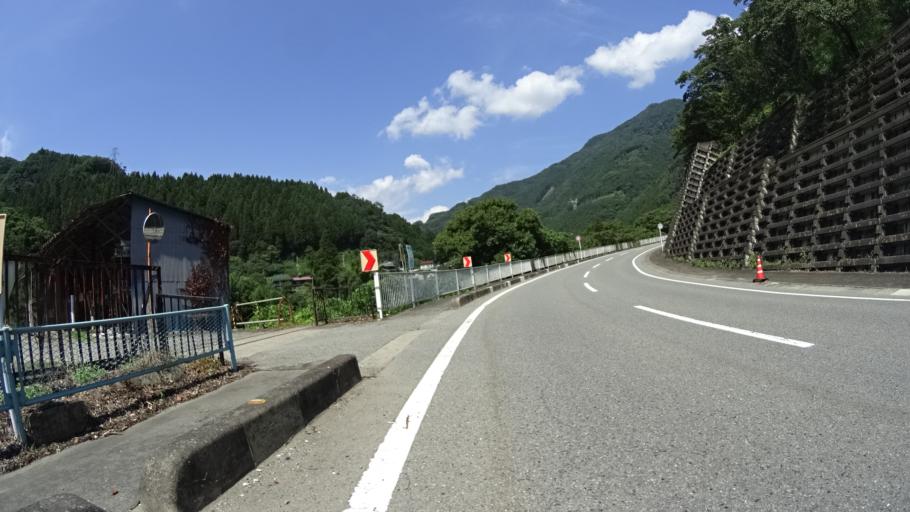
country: JP
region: Gunma
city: Tomioka
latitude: 36.0803
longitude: 138.7944
